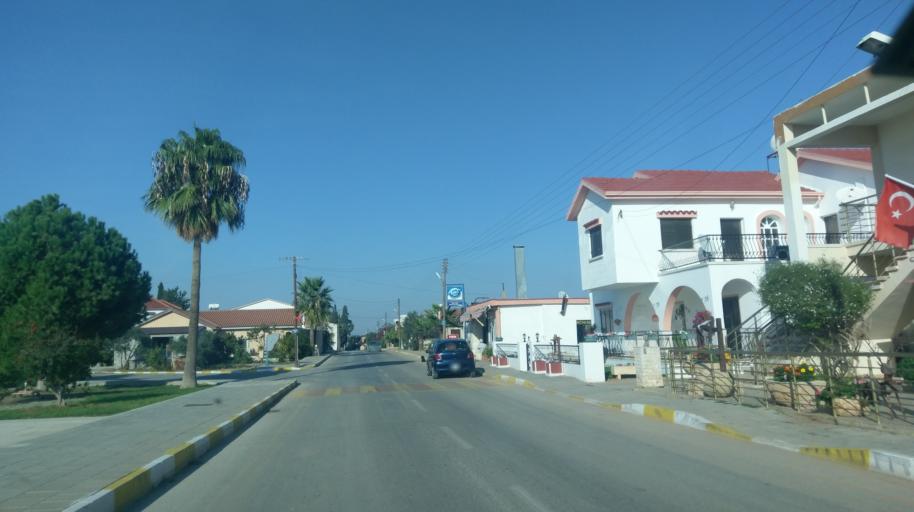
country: CY
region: Larnaka
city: Pergamos
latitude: 35.0444
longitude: 33.7086
